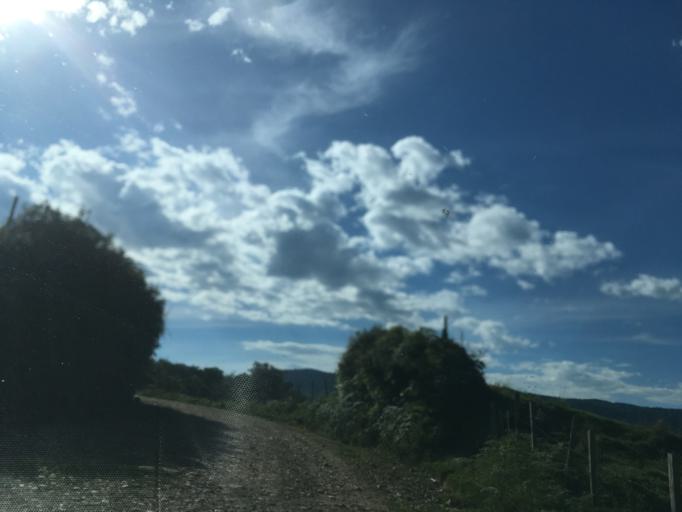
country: CO
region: Santander
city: Oiba
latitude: 6.1407
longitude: -73.1910
